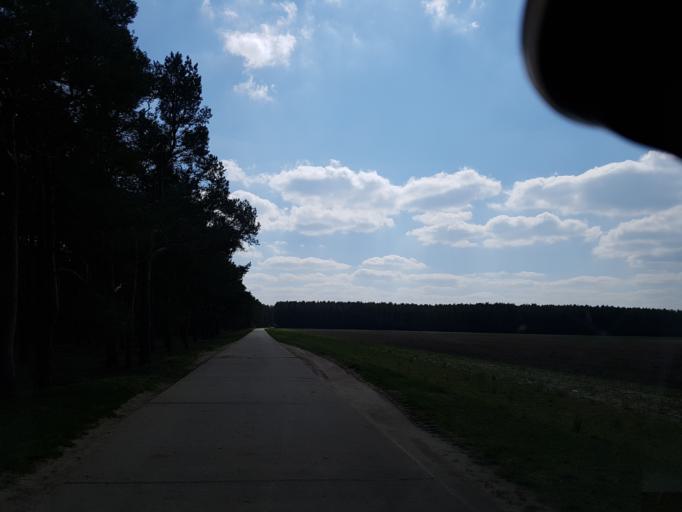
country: DE
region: Brandenburg
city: Bruck
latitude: 52.1894
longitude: 12.7478
